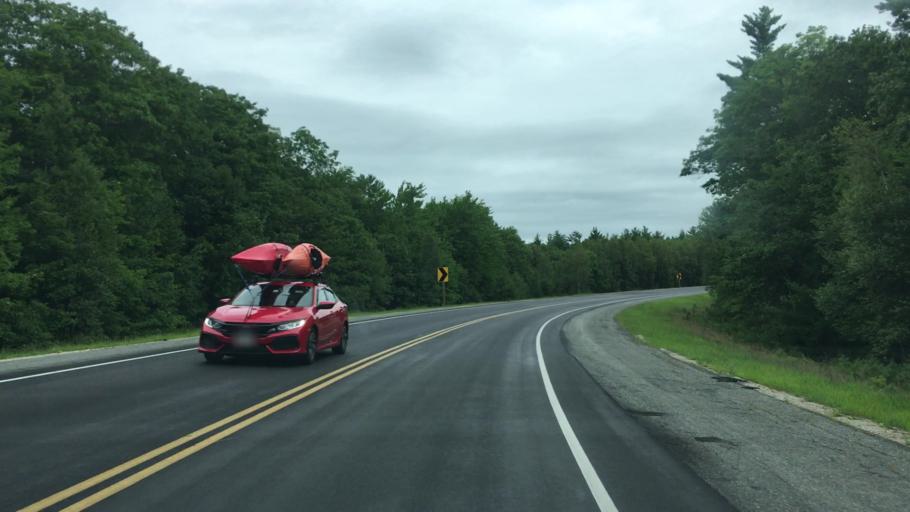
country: US
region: Maine
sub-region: Washington County
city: Cherryfield
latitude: 44.9081
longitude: -67.8571
